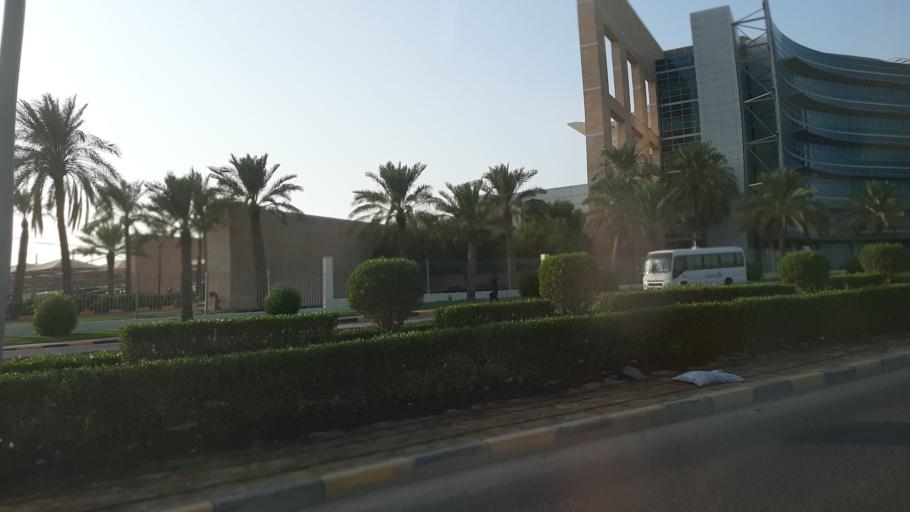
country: KW
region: Al Ahmadi
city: Al Ahmadi
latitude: 29.0918
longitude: 48.0882
